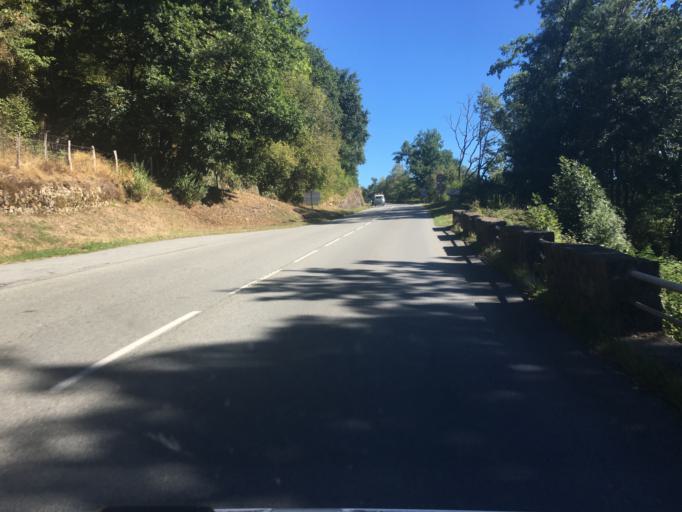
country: FR
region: Limousin
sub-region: Departement de la Correze
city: Bort-les-Orgues
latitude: 45.4049
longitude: 2.4968
